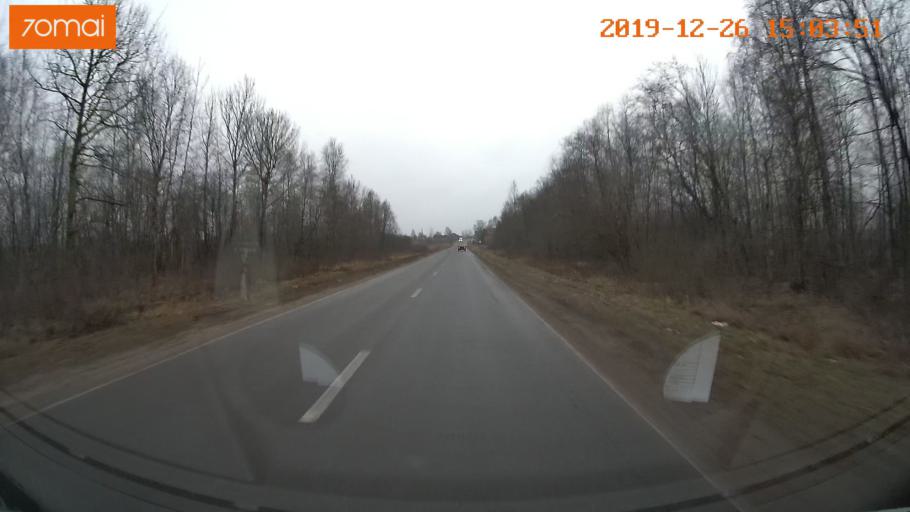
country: RU
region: Jaroslavl
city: Rybinsk
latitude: 58.2069
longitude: 38.8674
